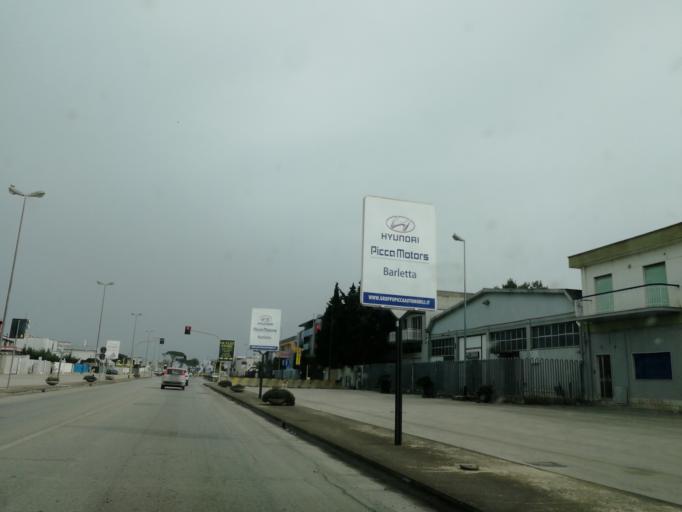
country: IT
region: Apulia
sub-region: Provincia di Barletta - Andria - Trani
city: Barletta
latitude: 41.3094
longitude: 16.3109
